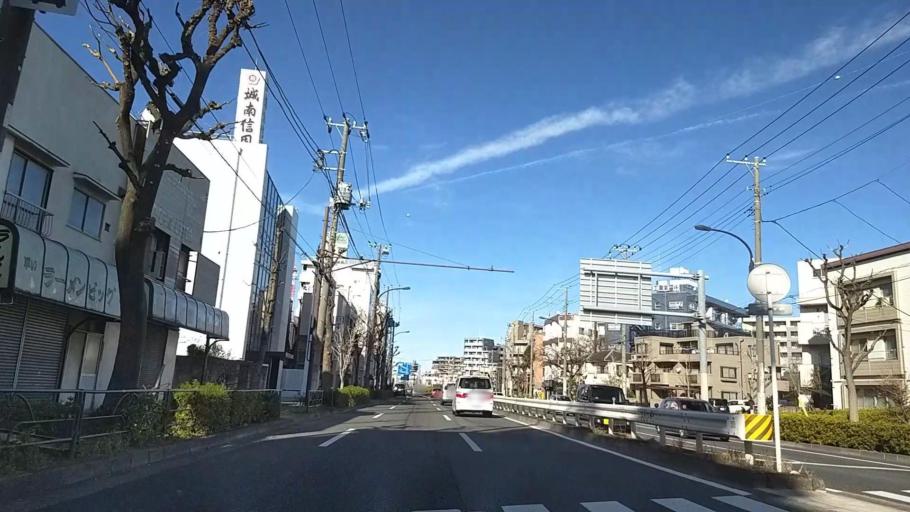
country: JP
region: Kanagawa
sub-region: Kawasaki-shi
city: Kawasaki
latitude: 35.5691
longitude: 139.6914
